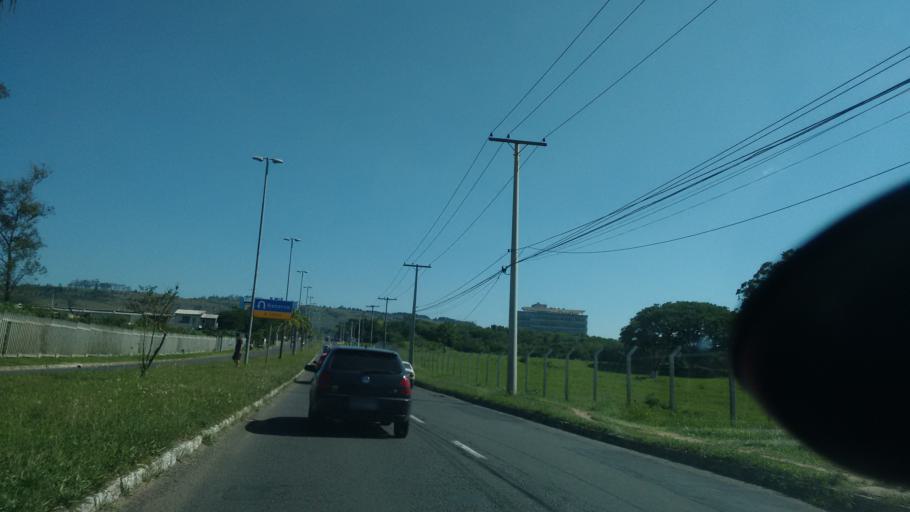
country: BR
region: Rio Grande do Sul
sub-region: Cachoeirinha
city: Cachoeirinha
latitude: -30.0283
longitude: -51.1206
